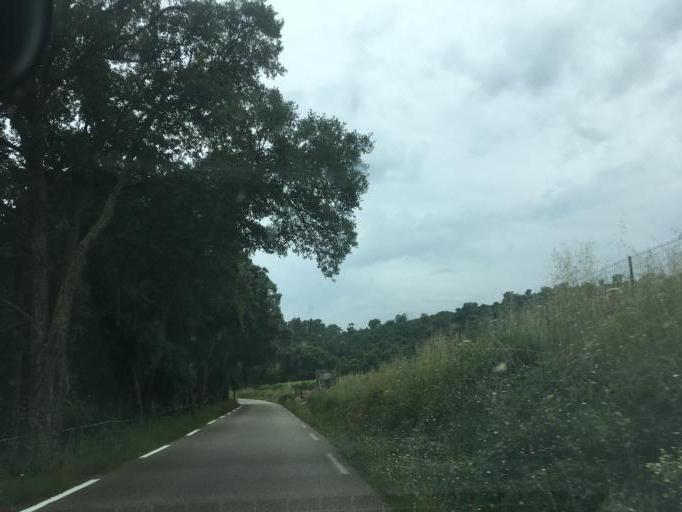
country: FR
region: Provence-Alpes-Cote d'Azur
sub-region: Departement du Var
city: La Londe-les-Maures
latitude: 43.1807
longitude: 6.2145
